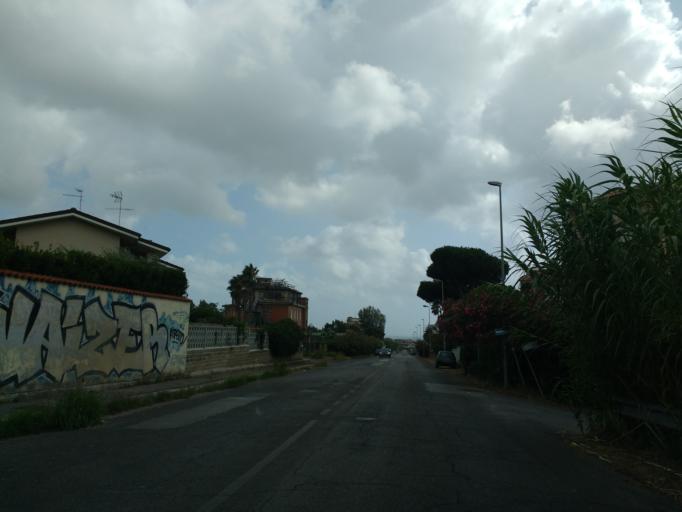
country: IT
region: Latium
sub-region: Citta metropolitana di Roma Capitale
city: Anzio
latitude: 41.4800
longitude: 12.6040
